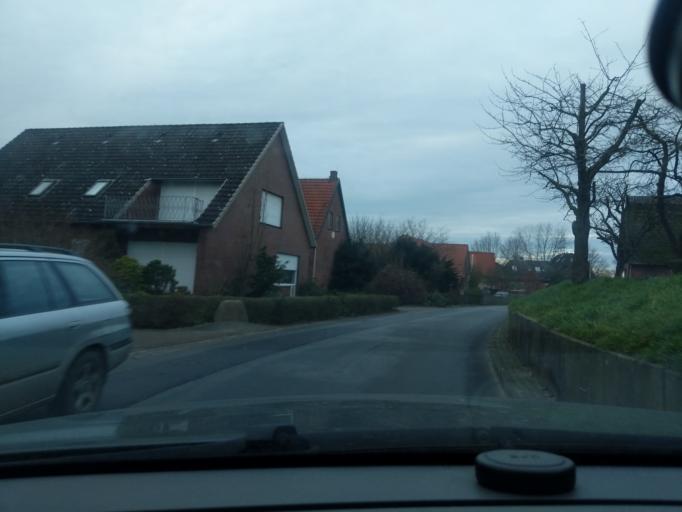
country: DE
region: Lower Saxony
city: Mittelnkirchen
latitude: 53.5340
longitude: 9.6124
